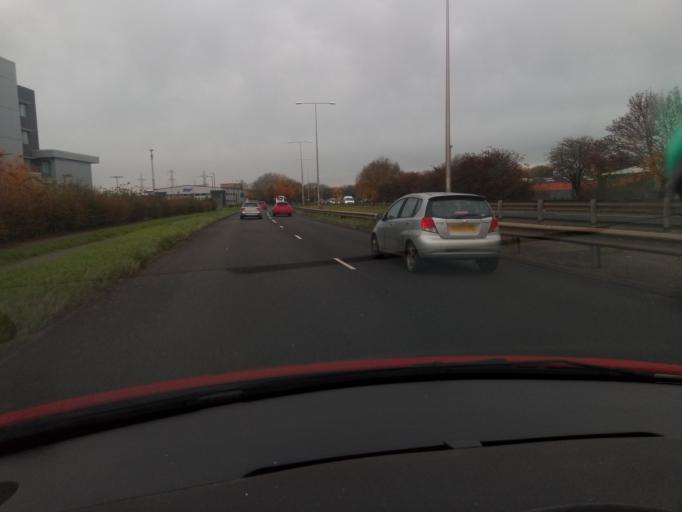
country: GB
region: England
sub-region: Derbyshire
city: Borrowash
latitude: 52.9076
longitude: -1.4309
